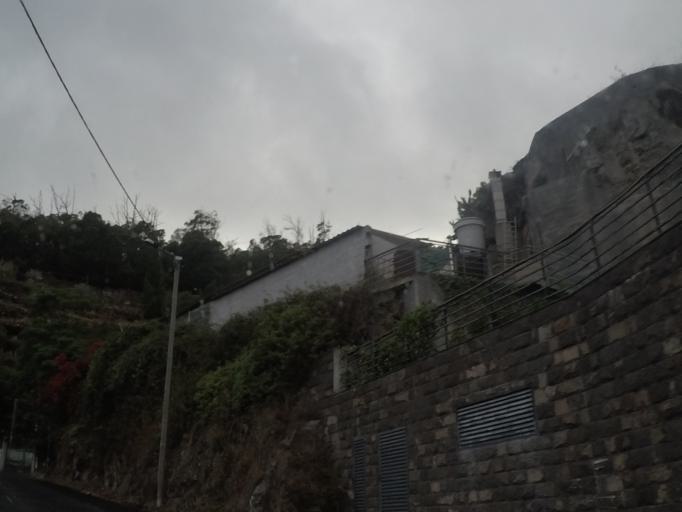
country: PT
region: Madeira
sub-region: Machico
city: Machico
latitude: 32.7071
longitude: -16.7785
